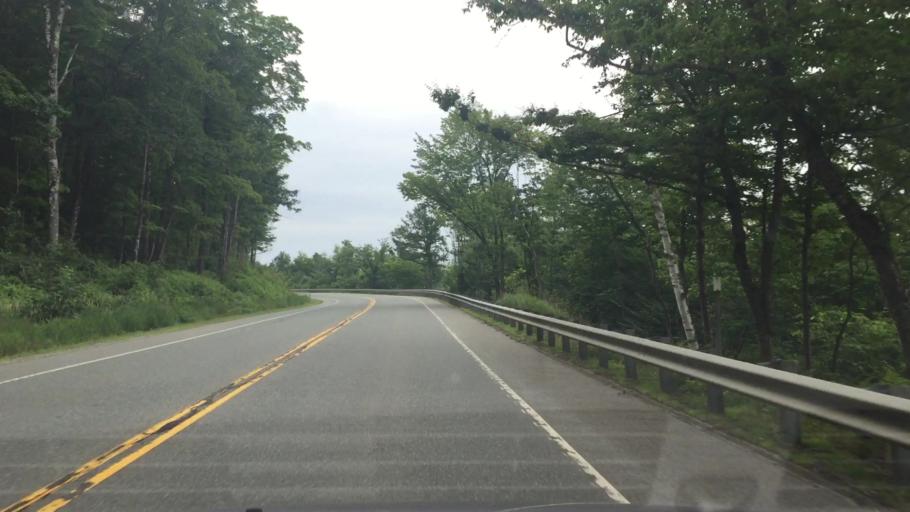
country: US
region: New Hampshire
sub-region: Grafton County
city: Deerfield
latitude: 44.2126
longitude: -71.6811
